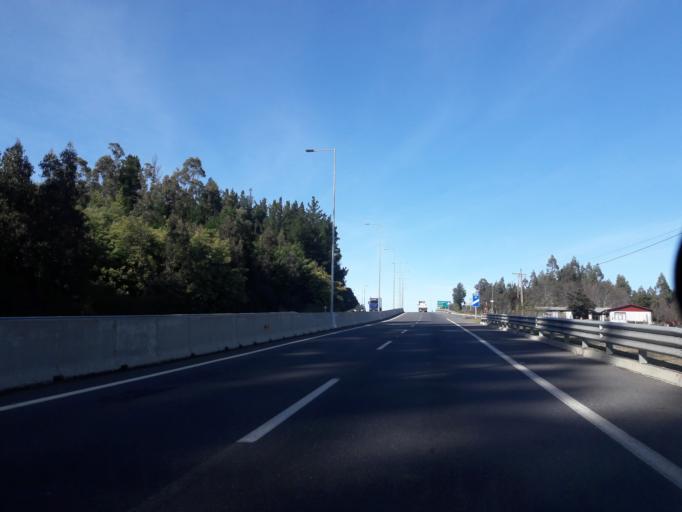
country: CL
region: Biobio
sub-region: Provincia de Concepcion
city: Chiguayante
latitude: -36.9301
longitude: -72.7661
